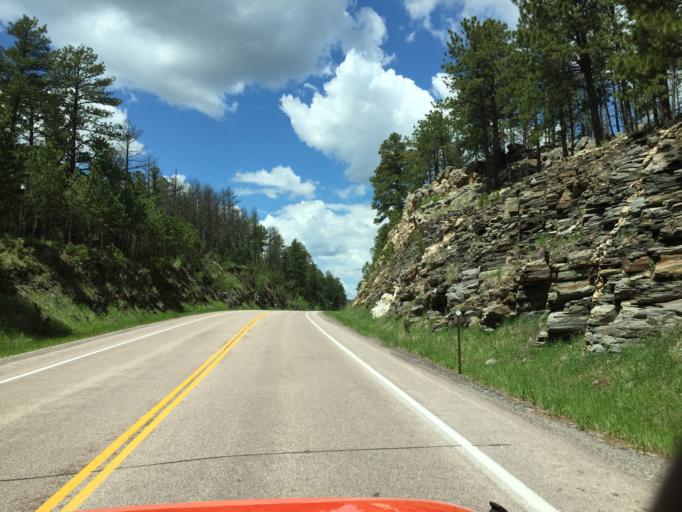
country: US
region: South Dakota
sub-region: Custer County
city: Custer
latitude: 43.8945
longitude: -103.5703
